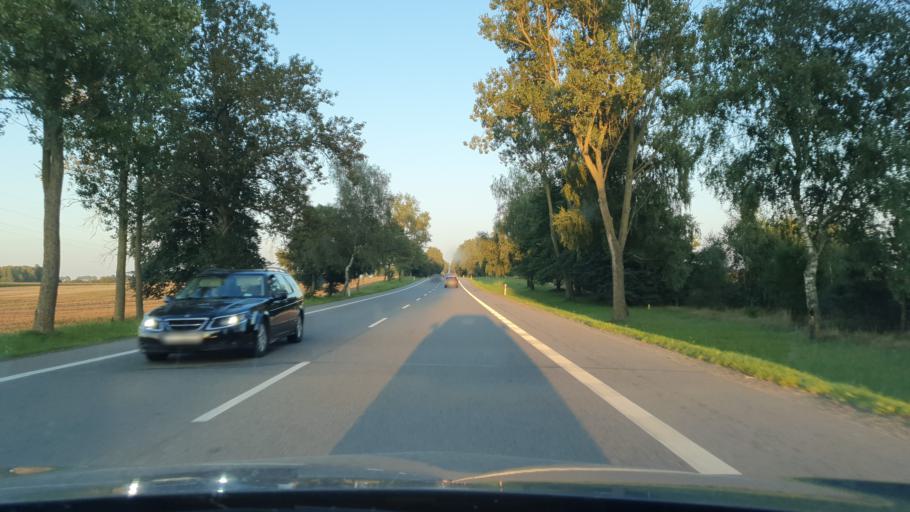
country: PL
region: Pomeranian Voivodeship
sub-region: Powiat slupski
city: Potegowo
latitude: 54.4770
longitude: 17.5045
